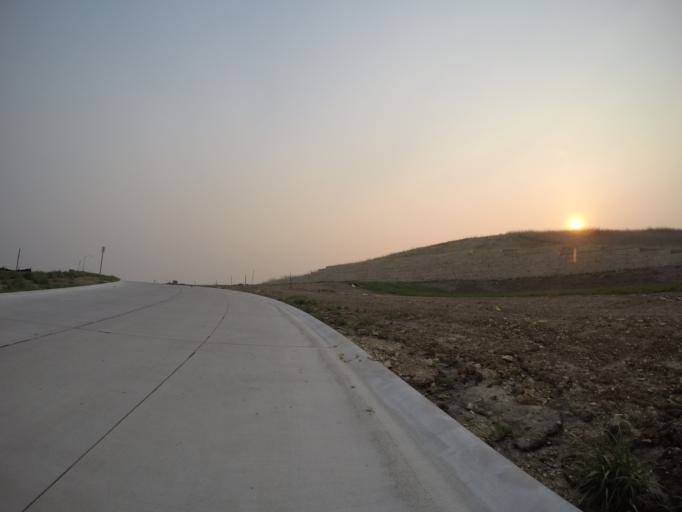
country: US
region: Kansas
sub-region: Riley County
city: Manhattan
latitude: 39.2212
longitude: -96.6442
